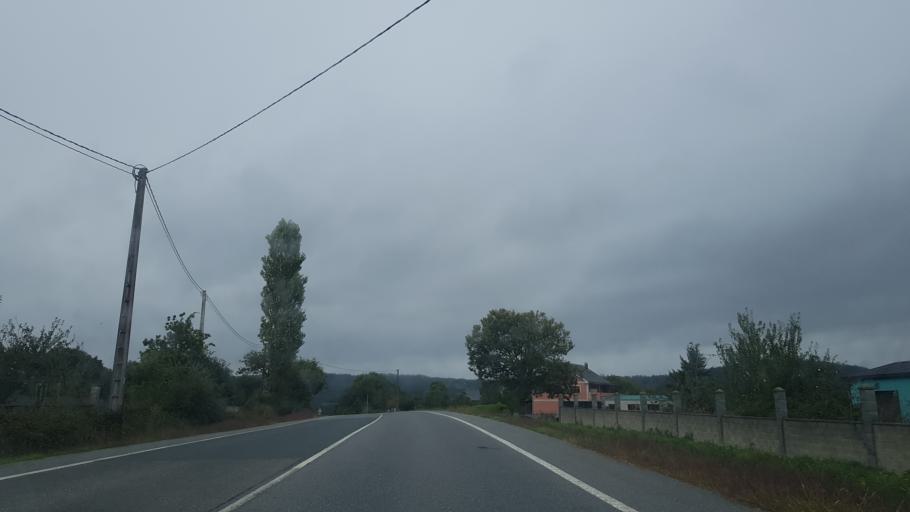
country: ES
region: Galicia
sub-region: Provincia de Lugo
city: Lugo
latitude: 42.9934
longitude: -7.6017
